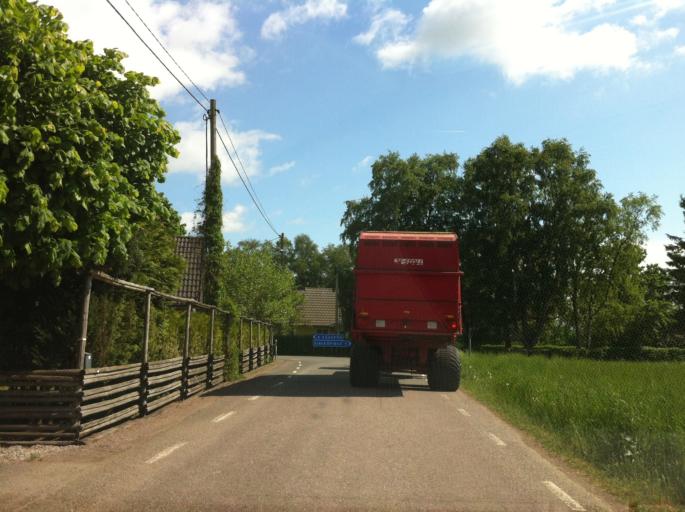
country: SE
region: Skane
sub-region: Landskrona
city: Asmundtorp
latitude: 55.9455
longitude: 12.9166
